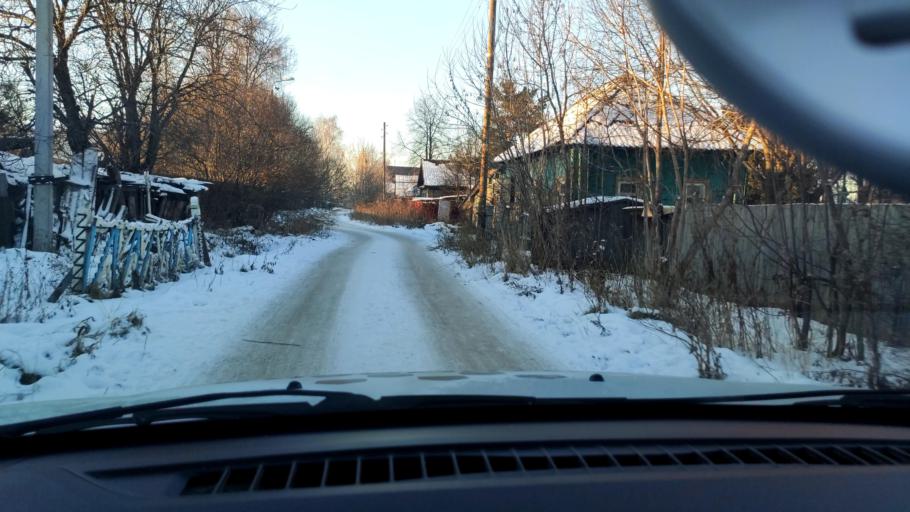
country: RU
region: Perm
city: Perm
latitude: 58.0521
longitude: 56.3361
